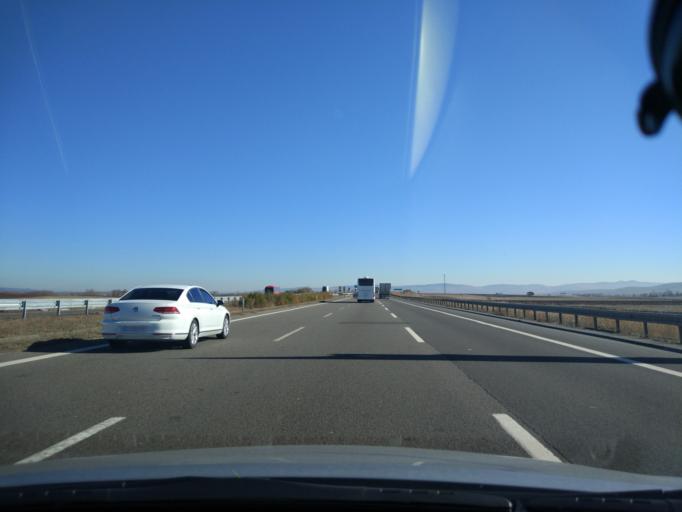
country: TR
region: Bolu
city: Dortdivan
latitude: 40.7464
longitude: 32.1007
